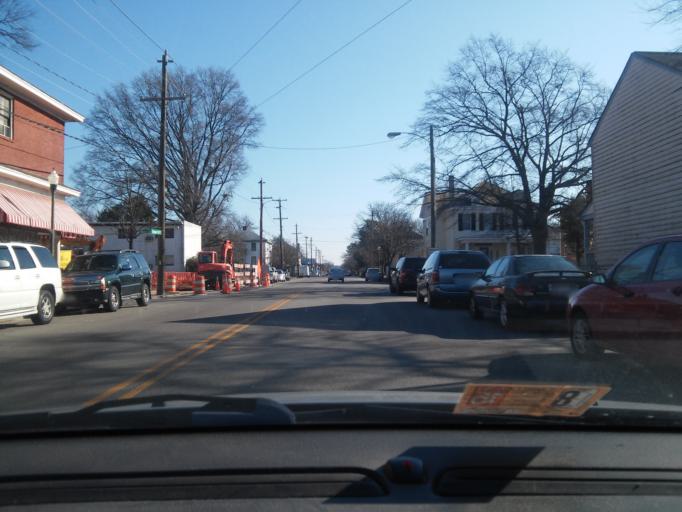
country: US
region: Virginia
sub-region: City of Richmond
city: Richmond
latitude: 37.5719
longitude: -77.4415
